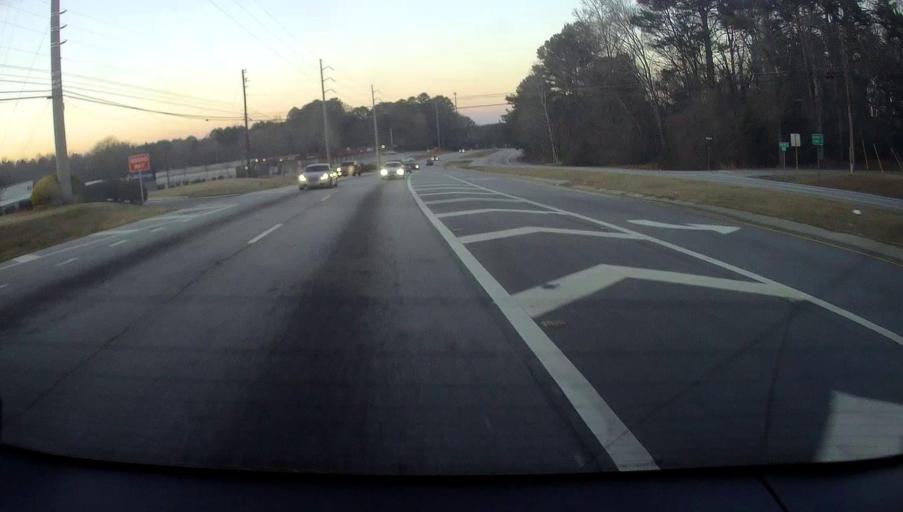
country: US
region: Georgia
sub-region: Clayton County
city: Riverdale
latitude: 33.5099
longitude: -84.4300
